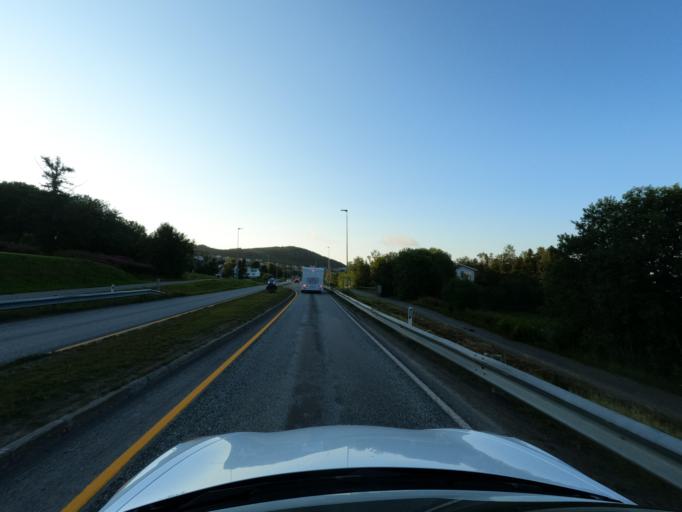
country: NO
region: Troms
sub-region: Harstad
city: Harstad
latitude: 68.7653
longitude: 16.5604
